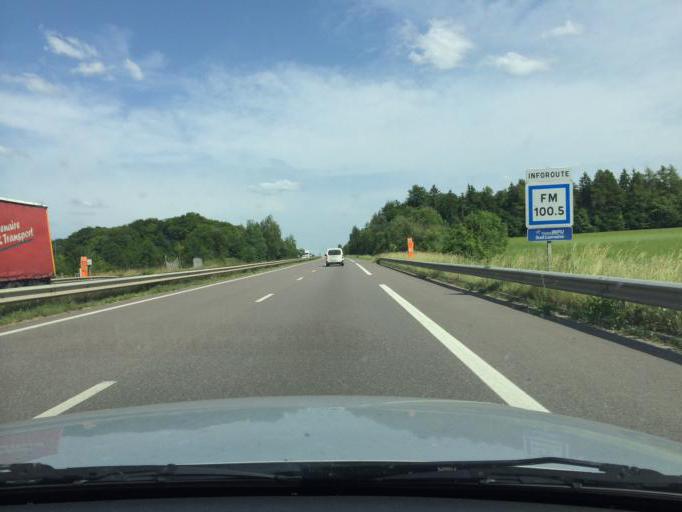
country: FR
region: Lorraine
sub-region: Departement de Meurthe-et-Moselle
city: Foug
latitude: 48.6770
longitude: 5.7593
